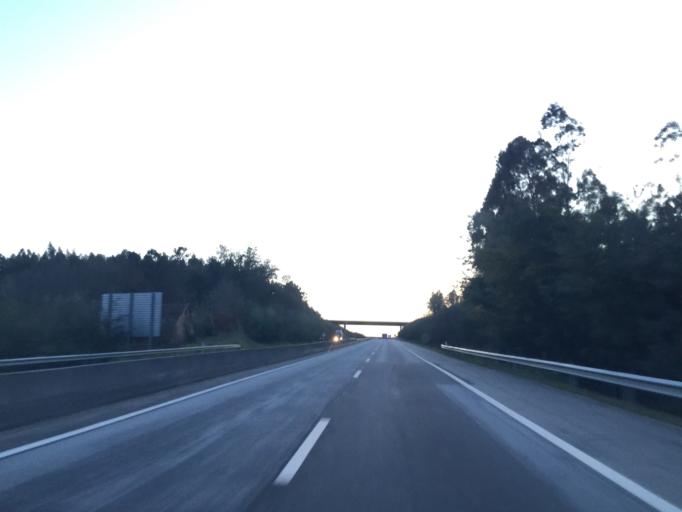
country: PT
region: Viseu
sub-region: Santa Comba Dao
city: Santa Comba Dao
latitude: 40.3928
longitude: -8.1031
